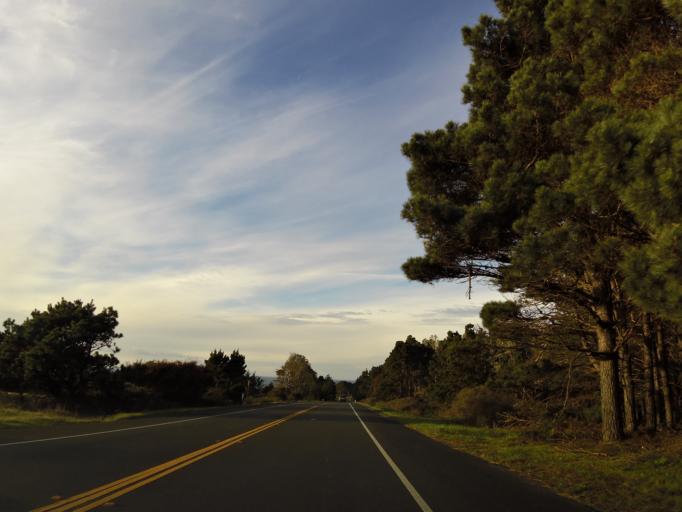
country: US
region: California
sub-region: Mendocino County
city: Fort Bragg
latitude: 39.3666
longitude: -123.8109
